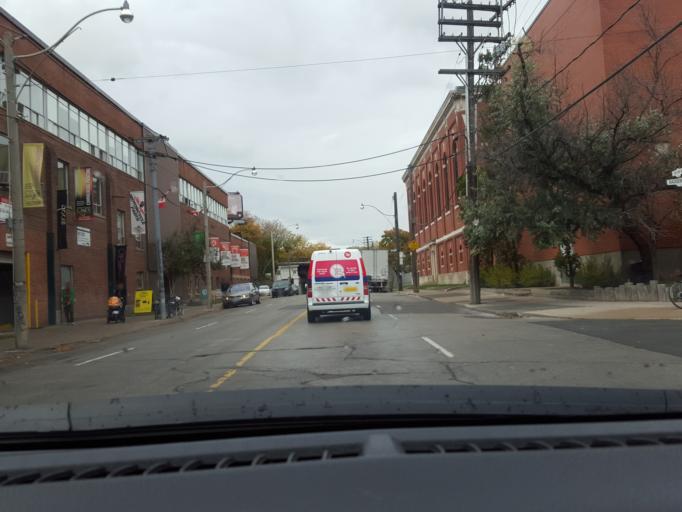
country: CA
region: Ontario
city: Toronto
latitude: 43.6661
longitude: -79.3421
